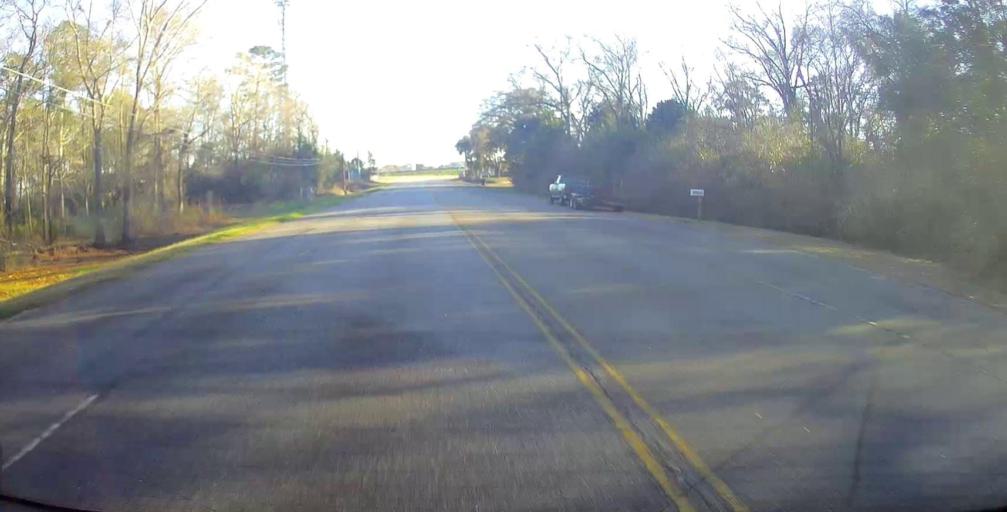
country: US
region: Georgia
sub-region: Dougherty County
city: Albany
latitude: 31.6258
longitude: -84.2293
